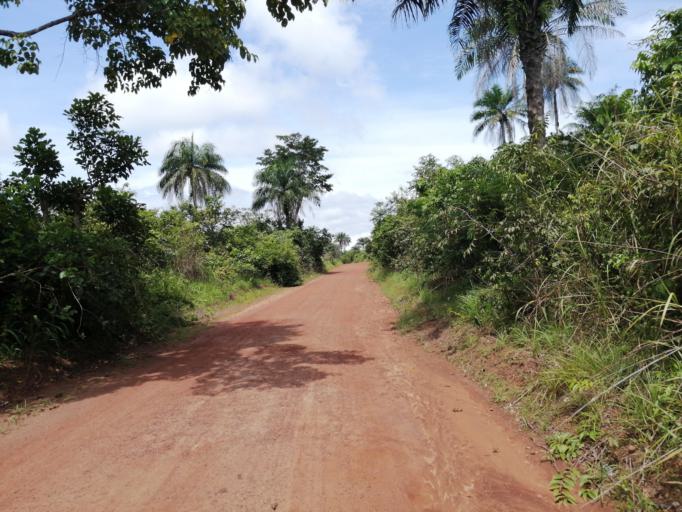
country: SL
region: Northern Province
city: Pepel
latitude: 8.6462
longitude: -13.0170
